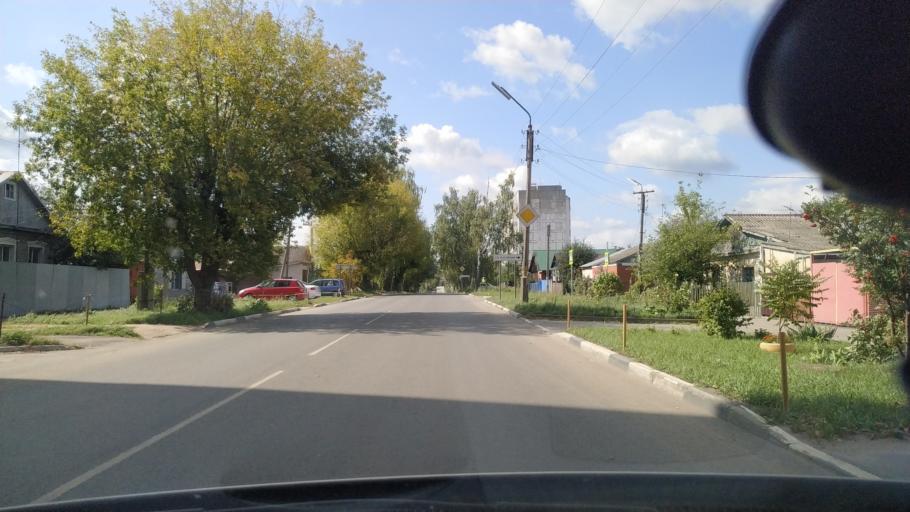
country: RU
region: Rjazan
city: Ryazan'
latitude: 54.6104
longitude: 39.7030
